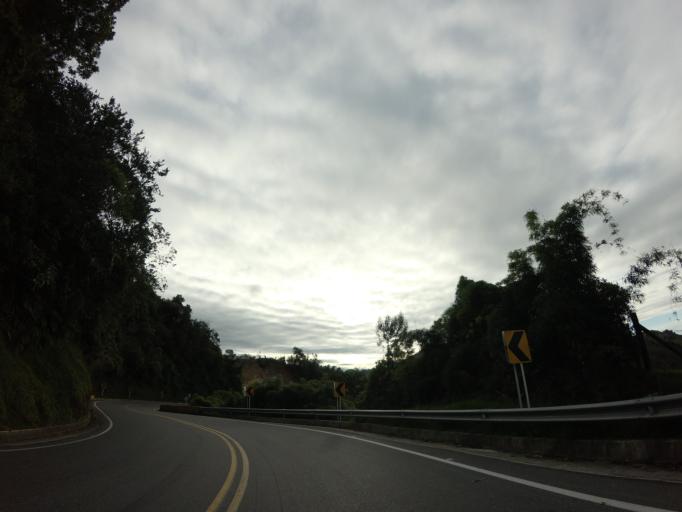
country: CO
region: Tolima
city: Herveo
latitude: 5.1049
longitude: -75.2443
